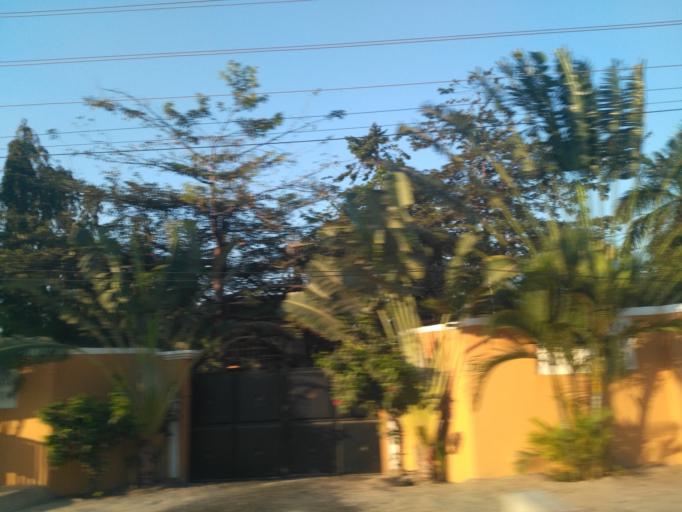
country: TZ
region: Dar es Salaam
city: Magomeni
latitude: -6.7583
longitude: 39.2352
